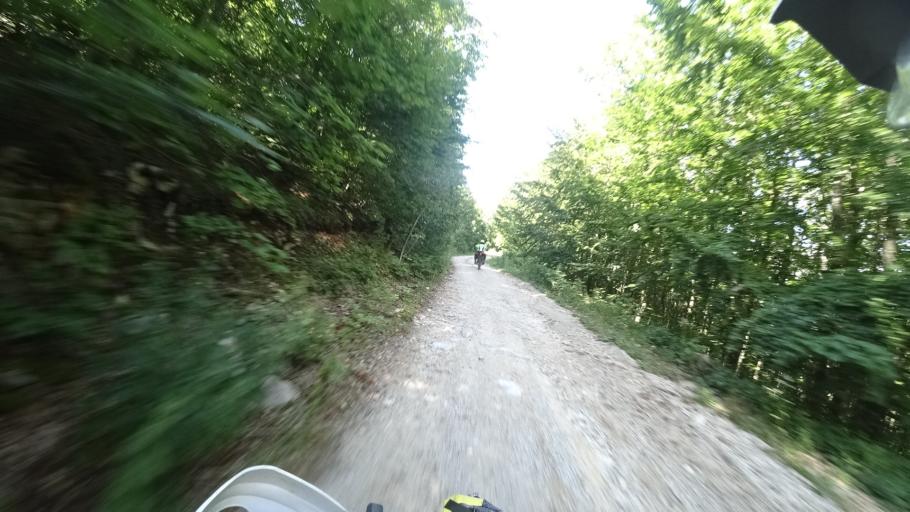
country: HR
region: Zadarska
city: Gracac
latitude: 44.4520
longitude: 15.9795
